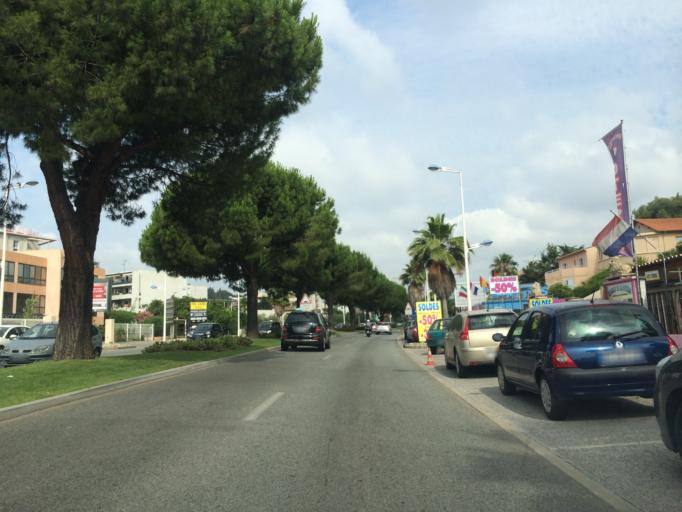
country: FR
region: Provence-Alpes-Cote d'Azur
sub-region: Departement des Alpes-Maritimes
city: Villeneuve-Loubet
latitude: 43.6604
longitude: 7.1358
